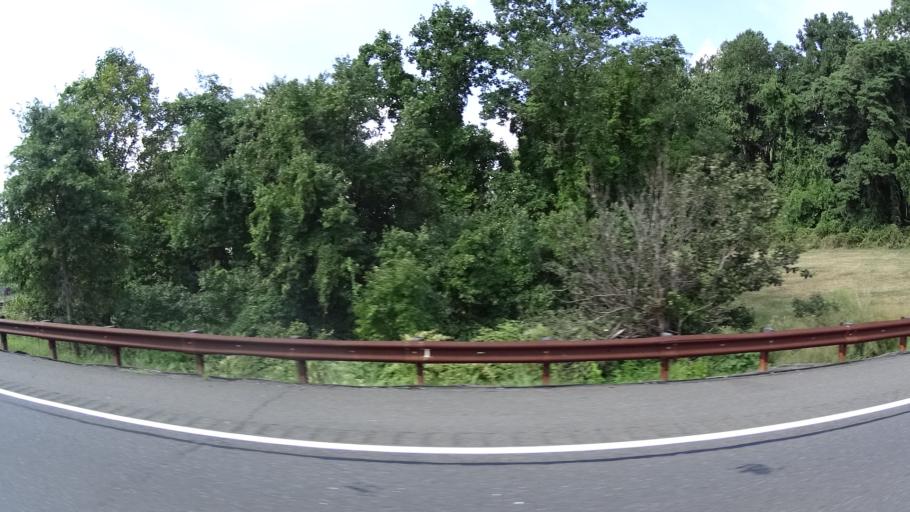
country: US
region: New Jersey
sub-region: Monmouth County
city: Strathmore
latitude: 40.3892
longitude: -74.1799
